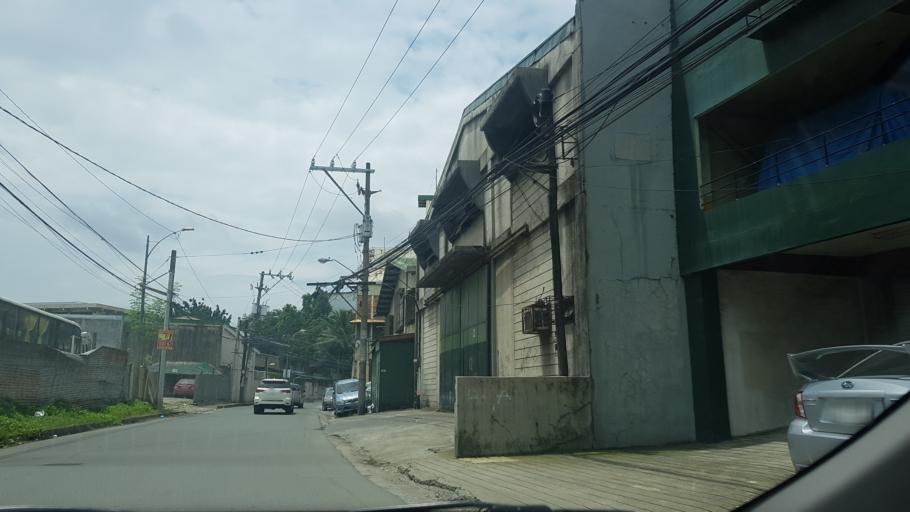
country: PH
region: Calabarzon
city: Del Monte
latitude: 14.6509
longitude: 121.0039
